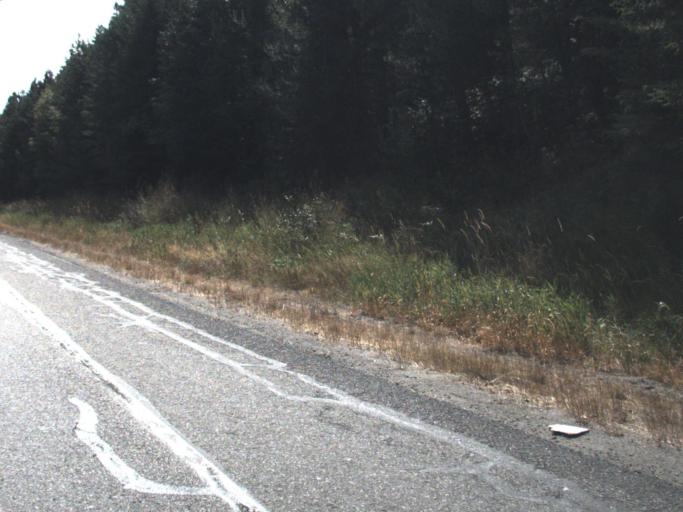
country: US
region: Washington
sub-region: Stevens County
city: Chewelah
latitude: 48.1289
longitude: -117.6529
